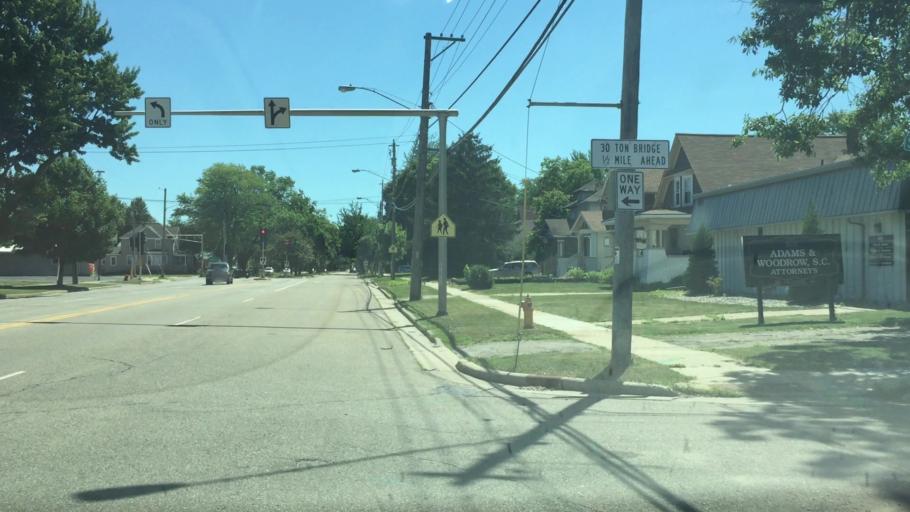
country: US
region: Wisconsin
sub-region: Winnebago County
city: Menasha
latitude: 44.1935
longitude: -88.4535
